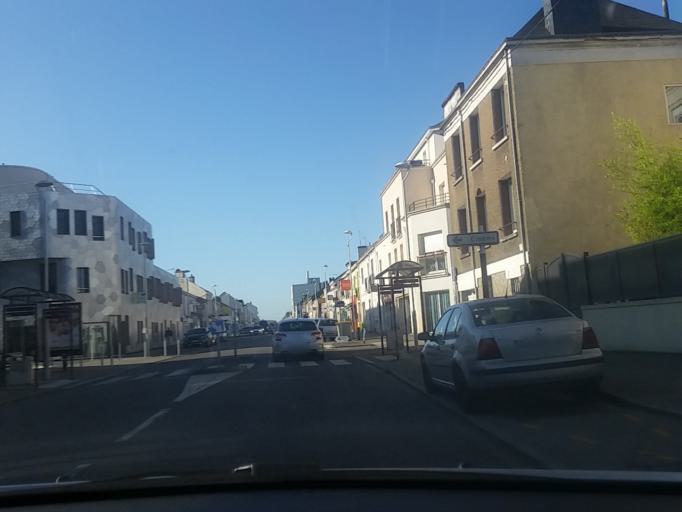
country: FR
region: Pays de la Loire
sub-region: Departement de la Loire-Atlantique
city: Reze
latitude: 47.1834
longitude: -1.5460
